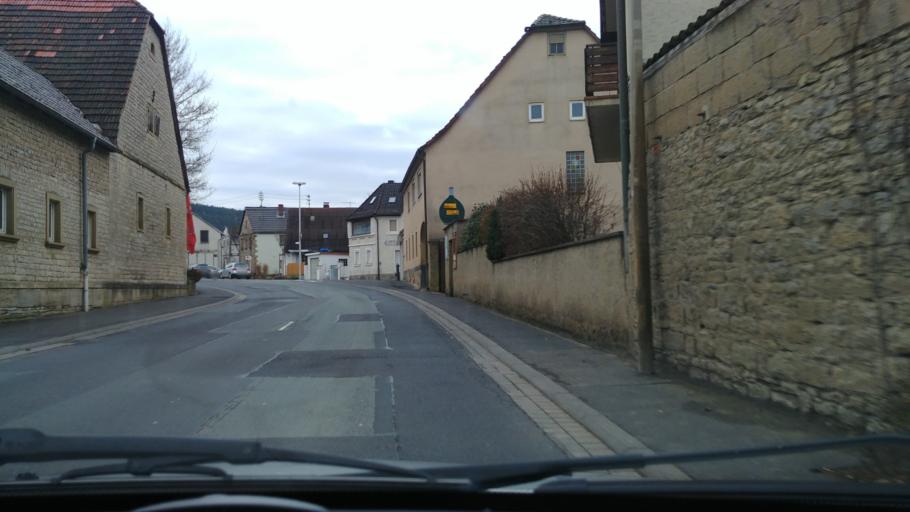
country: DE
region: Bavaria
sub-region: Regierungsbezirk Unterfranken
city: Thungen
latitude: 49.9515
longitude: 9.8879
